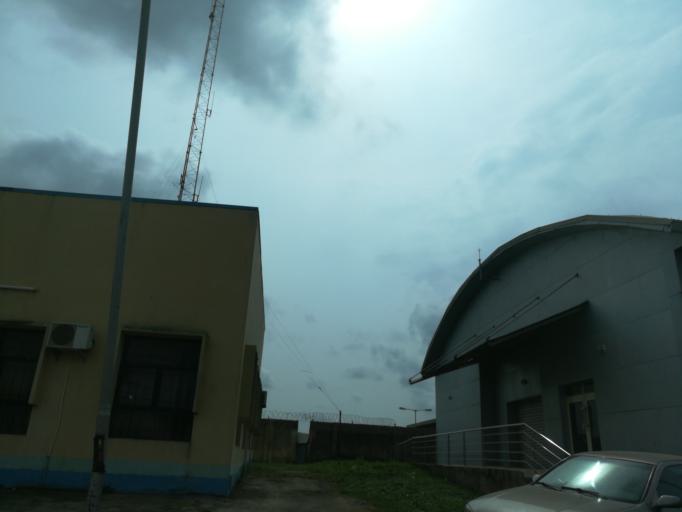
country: NG
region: Lagos
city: Oshodi
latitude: 6.5800
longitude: 3.3254
